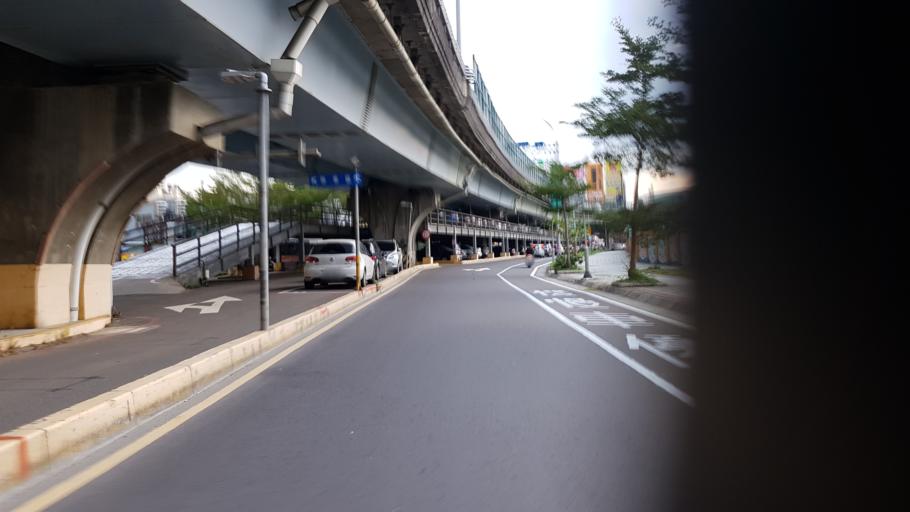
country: TW
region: Taiwan
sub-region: Hsinchu
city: Hsinchu
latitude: 24.7889
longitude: 121.0110
